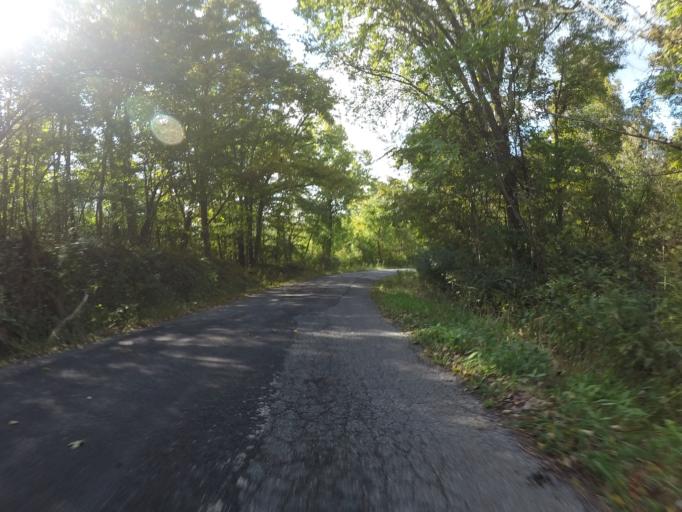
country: US
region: West Virginia
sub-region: Wayne County
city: Lavalette
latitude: 38.3676
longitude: -82.4742
